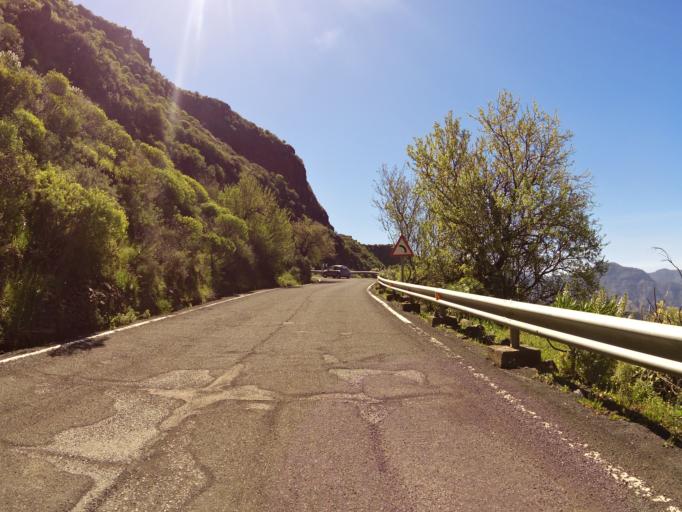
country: ES
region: Canary Islands
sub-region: Provincia de Las Palmas
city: Artenara
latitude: 28.0091
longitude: -15.6879
